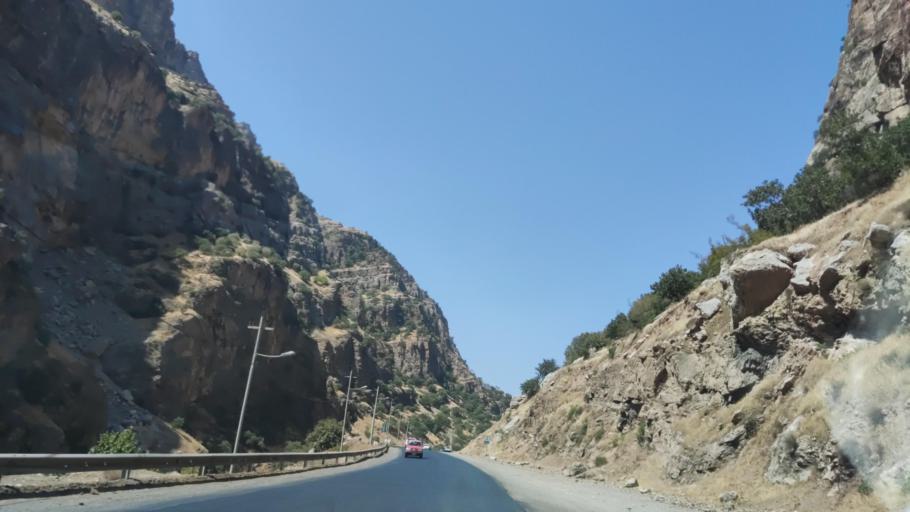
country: IQ
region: Arbil
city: Ruwandiz
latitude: 36.6312
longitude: 44.4860
